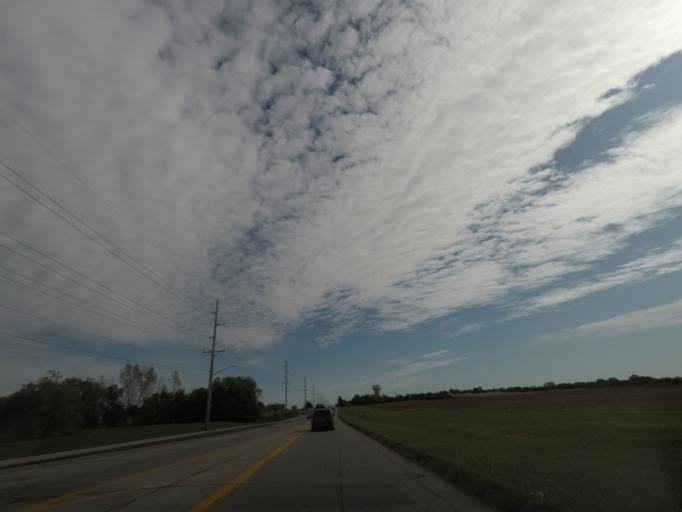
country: US
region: Iowa
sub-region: Story County
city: Ames
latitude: 42.0120
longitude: -93.6689
